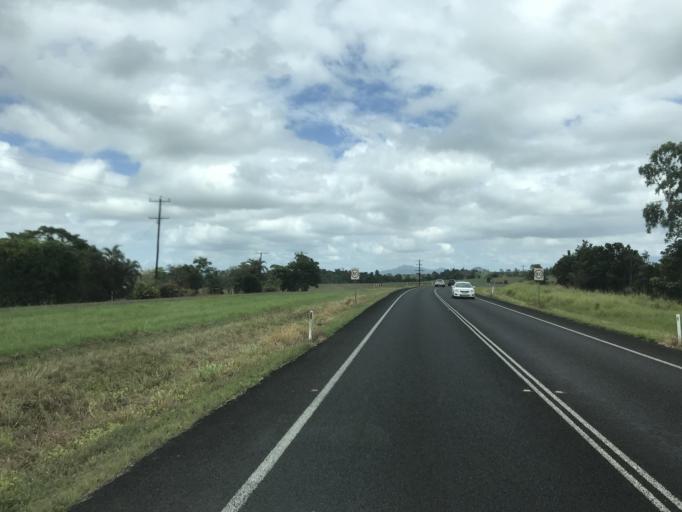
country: AU
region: Queensland
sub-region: Cassowary Coast
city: Innisfail
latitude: -17.5771
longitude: 145.9623
